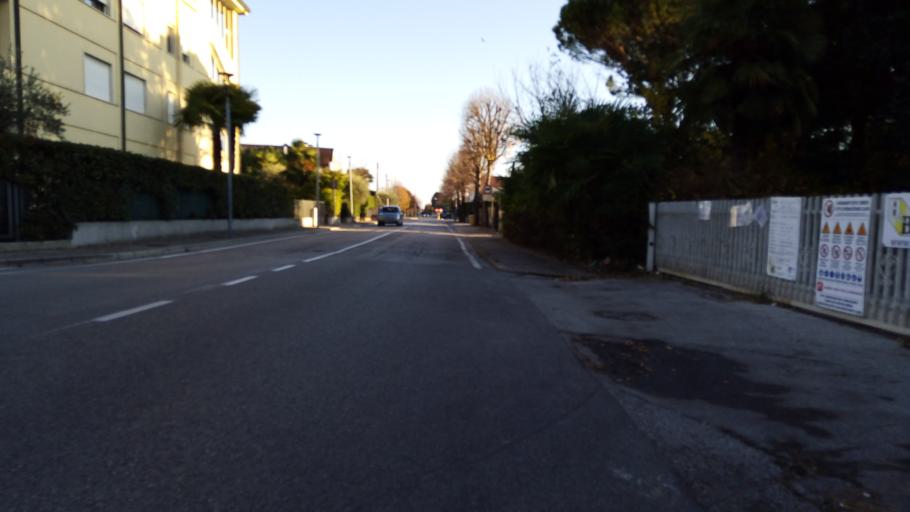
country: IT
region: Veneto
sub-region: Provincia di Padova
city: Abano Terme
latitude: 45.3459
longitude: 11.7837
